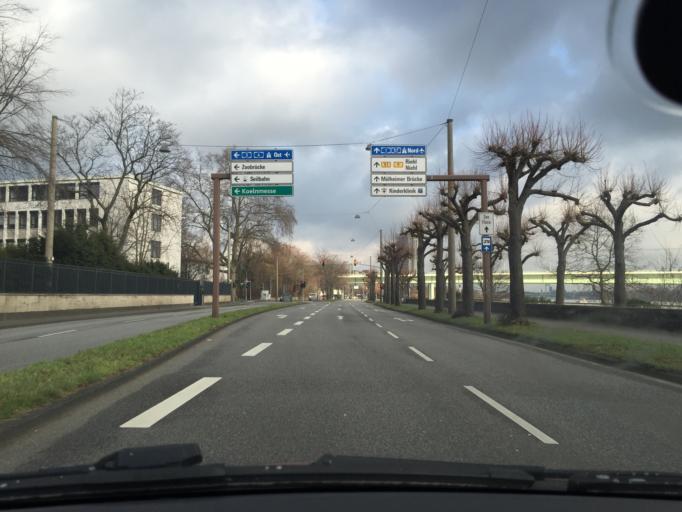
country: DE
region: North Rhine-Westphalia
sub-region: Regierungsbezirk Koln
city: Riehl
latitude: 50.9535
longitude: 6.9700
